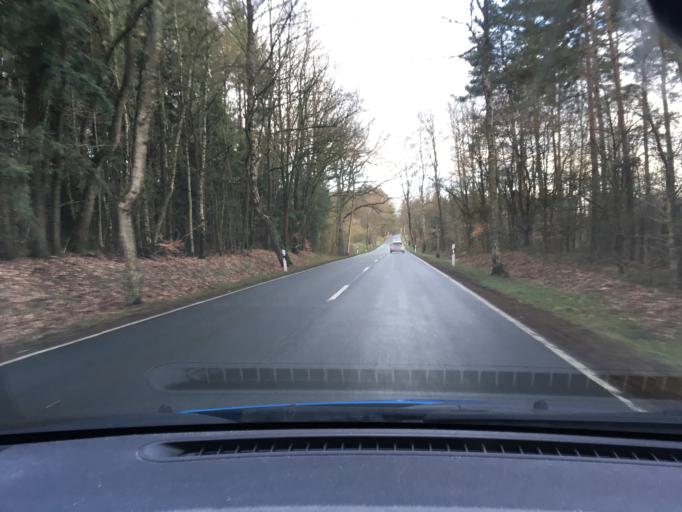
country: DE
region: Lower Saxony
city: Hanstedt
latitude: 53.2261
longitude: 10.0239
